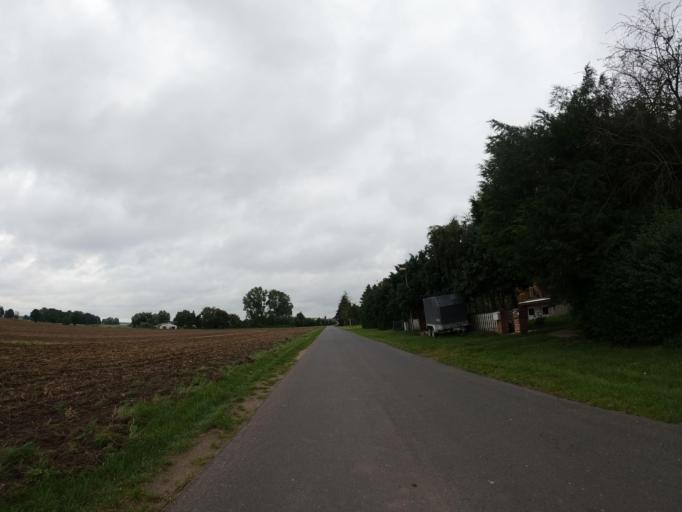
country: DE
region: Mecklenburg-Vorpommern
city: Poseritz
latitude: 54.2737
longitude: 13.2536
